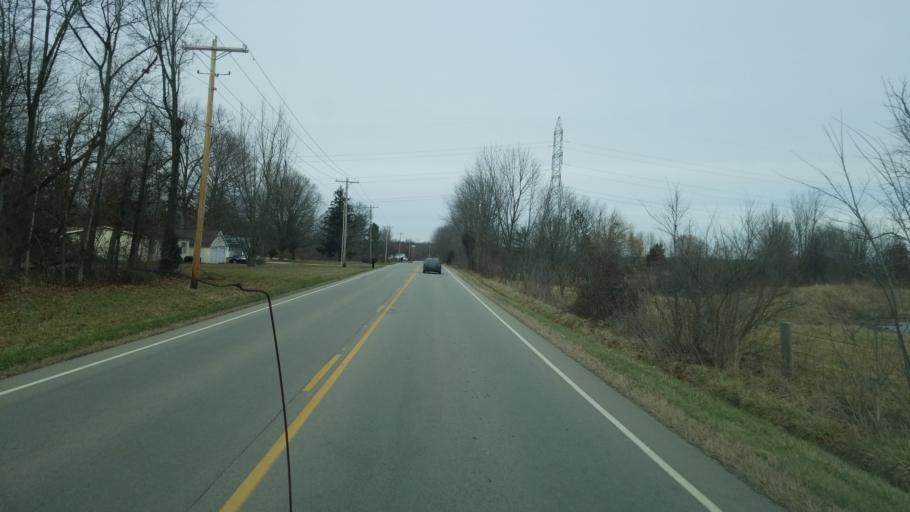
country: US
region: Ohio
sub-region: Adams County
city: Winchester
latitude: 39.0286
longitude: -83.7050
